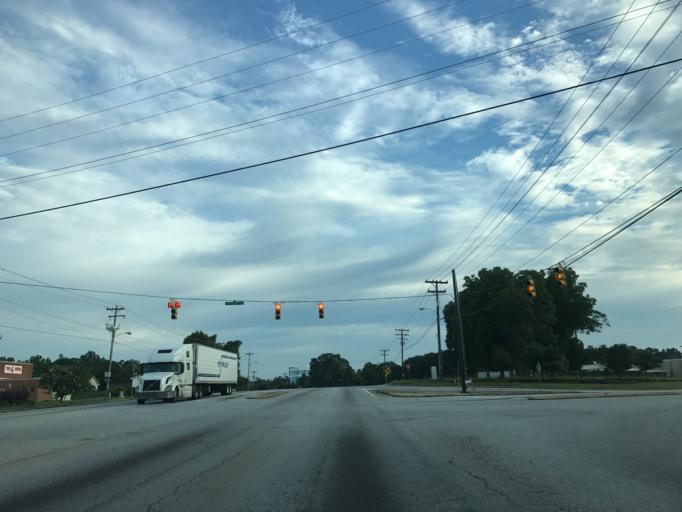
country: US
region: South Carolina
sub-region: Greenville County
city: Mauldin
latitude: 34.7994
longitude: -82.3161
